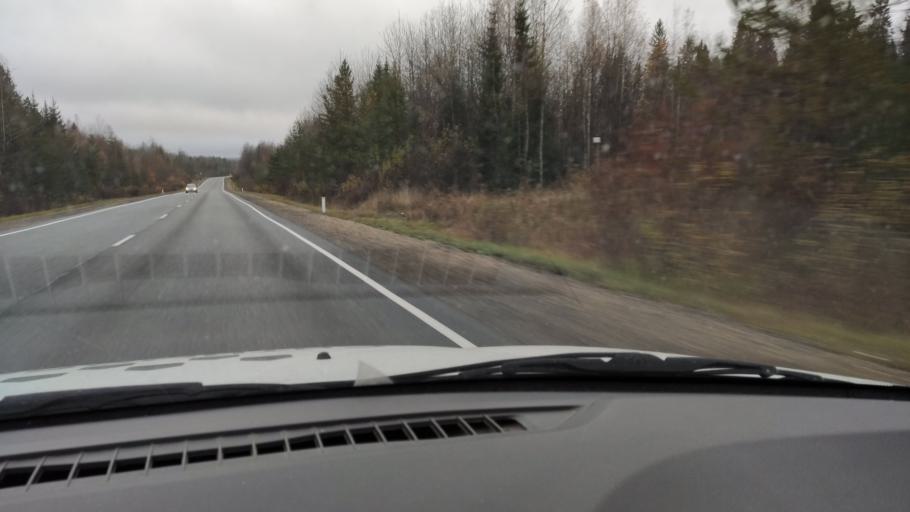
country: RU
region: Kirov
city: Omutninsk
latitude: 58.7041
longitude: 52.1078
